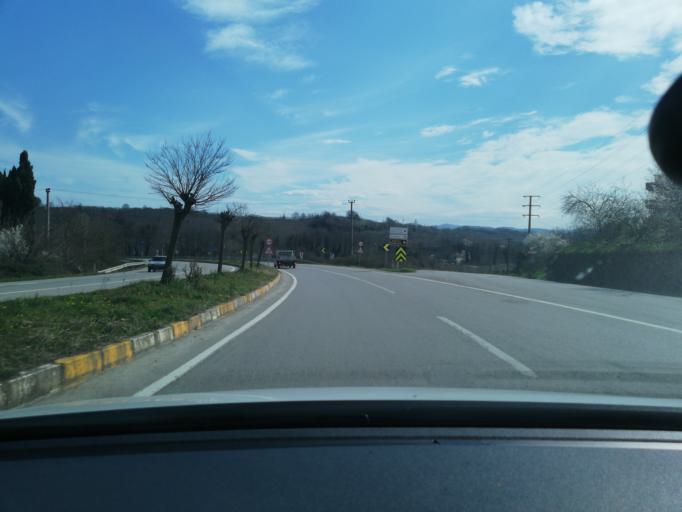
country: TR
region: Duzce
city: Akcakoca
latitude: 41.0831
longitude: 31.1448
